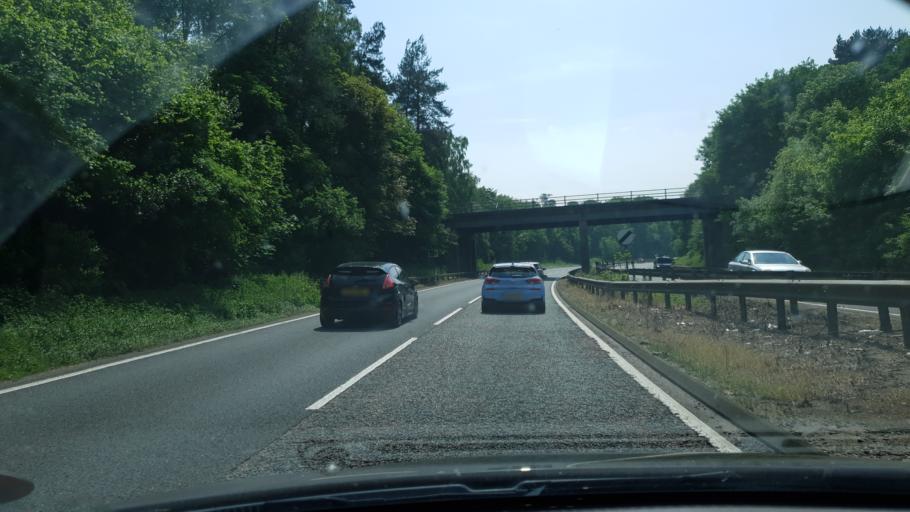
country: GB
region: England
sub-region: Suffolk
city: East Bergholt
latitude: 51.9609
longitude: 0.9720
